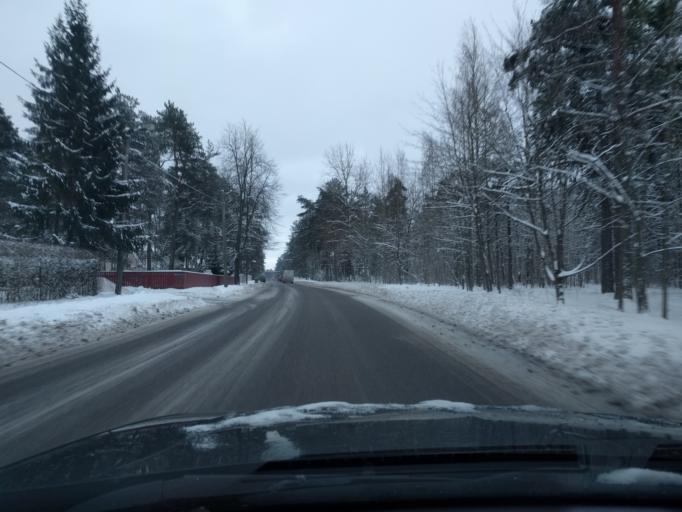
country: EE
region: Harju
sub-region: Saue vald
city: Laagri
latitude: 59.3778
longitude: 24.6701
